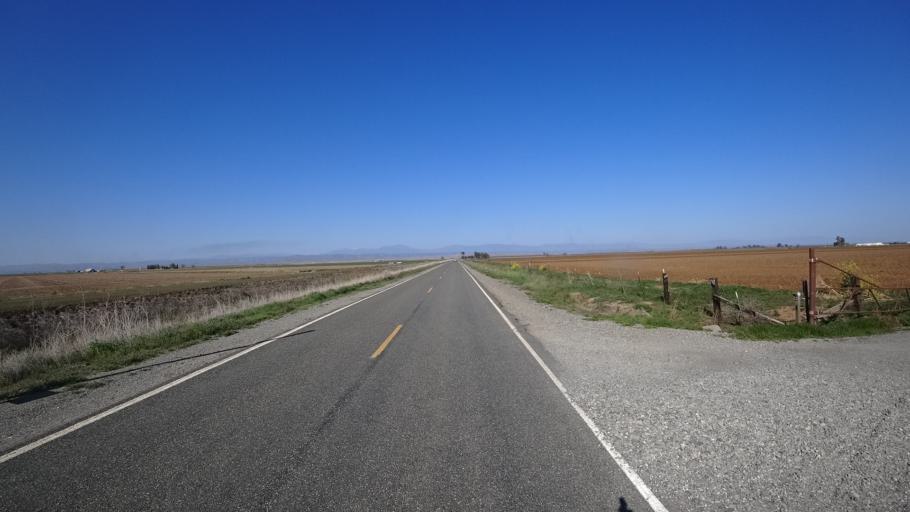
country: US
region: California
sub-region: Glenn County
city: Willows
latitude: 39.4949
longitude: -122.2260
